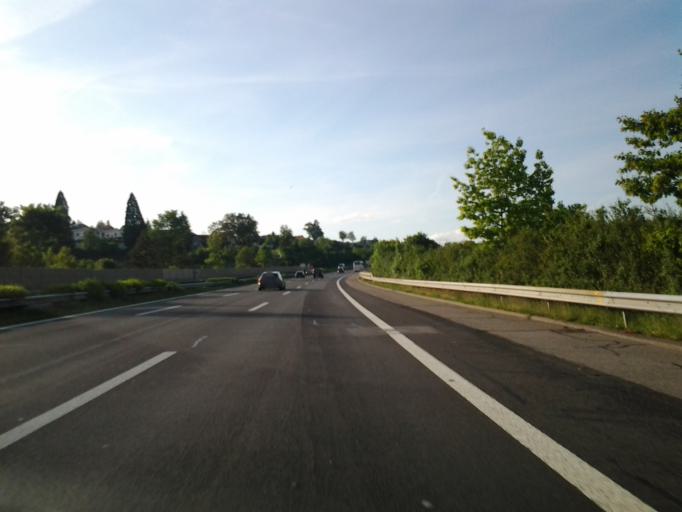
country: CH
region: Lucerne
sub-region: Sursee District
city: Knutwil
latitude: 47.1845
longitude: 8.0799
